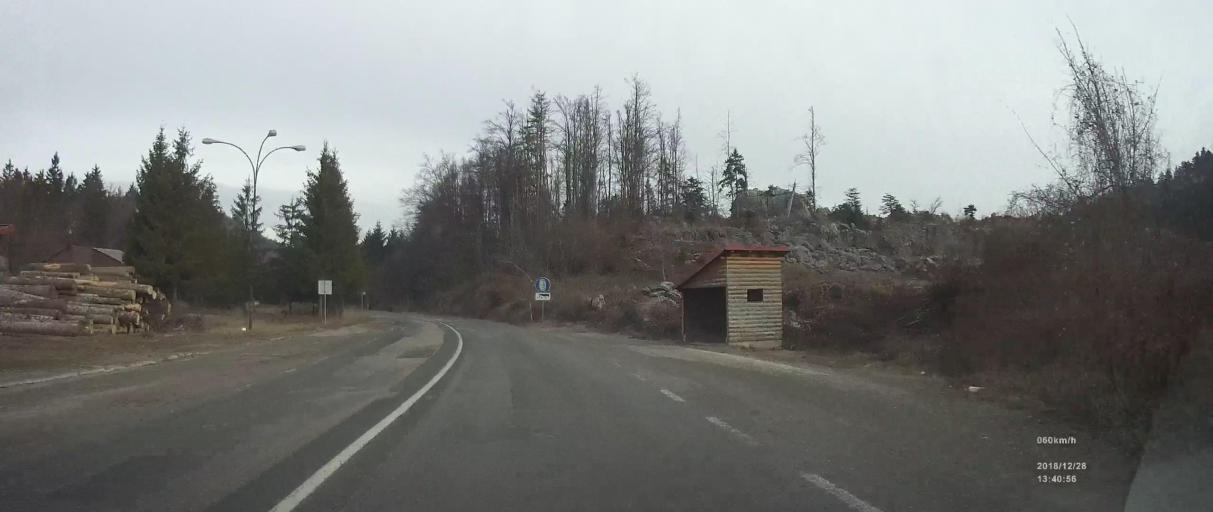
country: HR
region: Primorsko-Goranska
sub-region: Grad Delnice
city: Delnice
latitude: 45.3508
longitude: 14.7545
